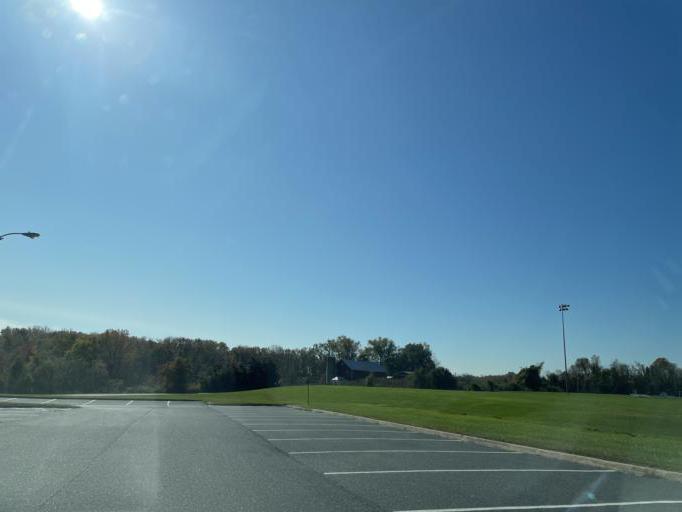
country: US
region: Maryland
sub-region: Harford County
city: Edgewood
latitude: 39.4188
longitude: -76.3138
